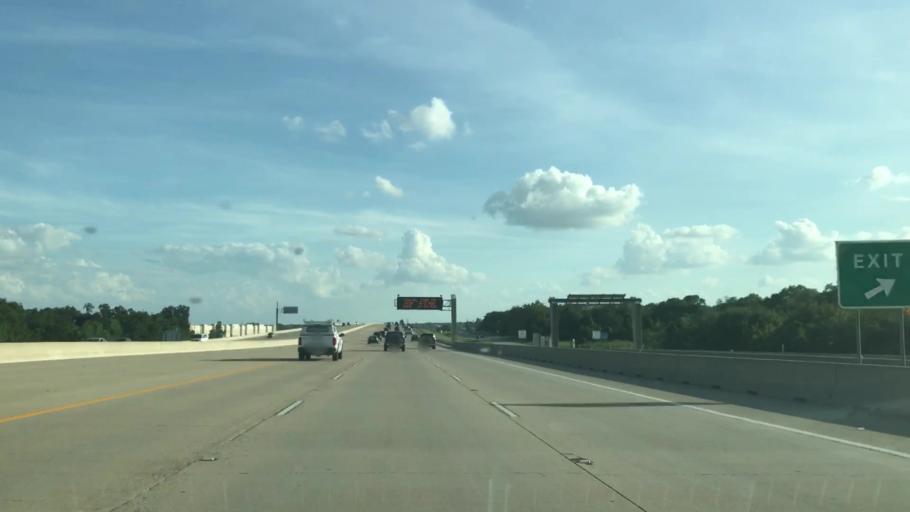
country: US
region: Texas
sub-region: Dallas County
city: Grand Prairie
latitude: 32.8077
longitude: -97.0185
